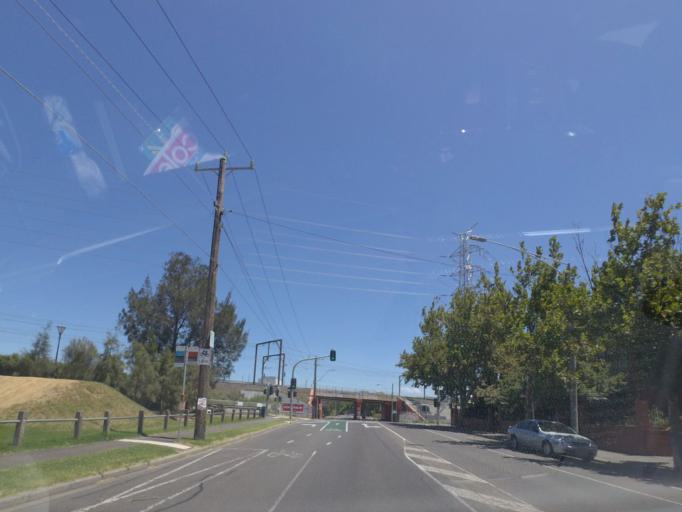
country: AU
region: Victoria
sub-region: Moonee Valley
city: Flemington
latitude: -37.7982
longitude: 144.9208
